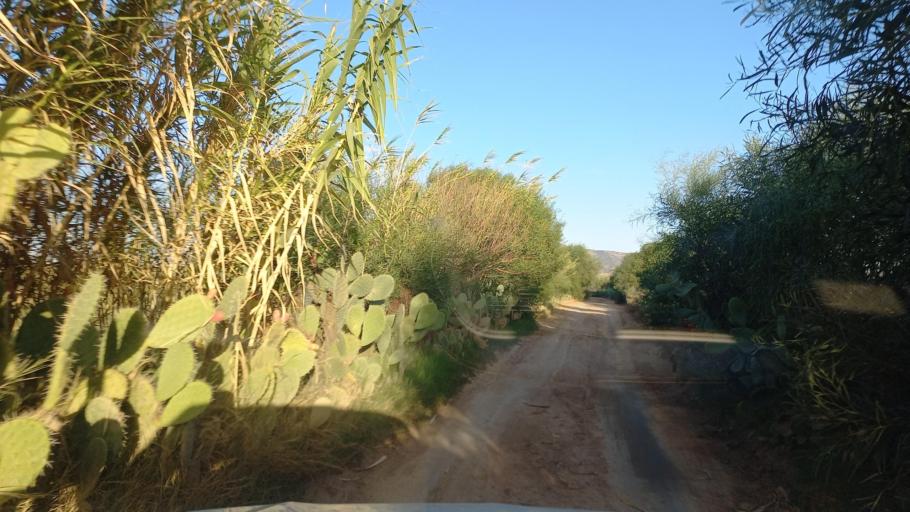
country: TN
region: Al Qasrayn
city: Sbiba
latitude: 35.4197
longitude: 9.1264
